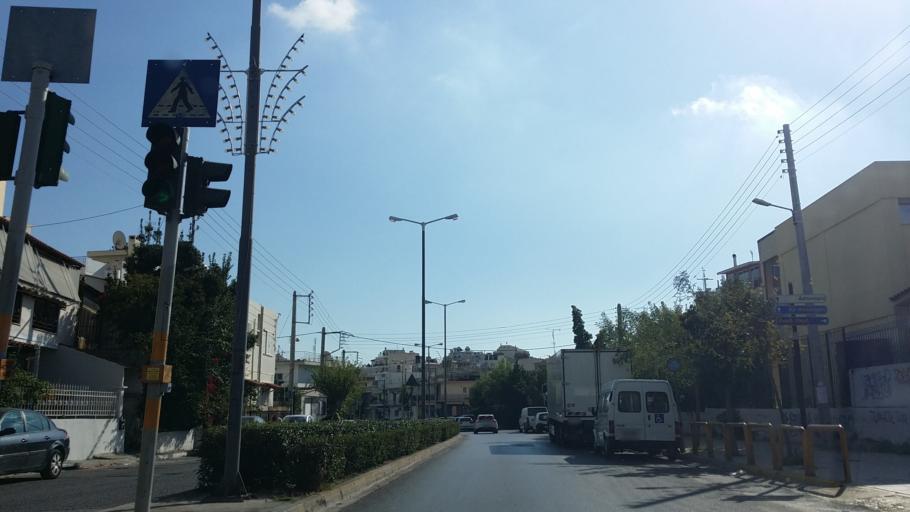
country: GR
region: Attica
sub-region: Nomarchia Athinas
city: Ilion
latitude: 38.0243
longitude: 23.7032
